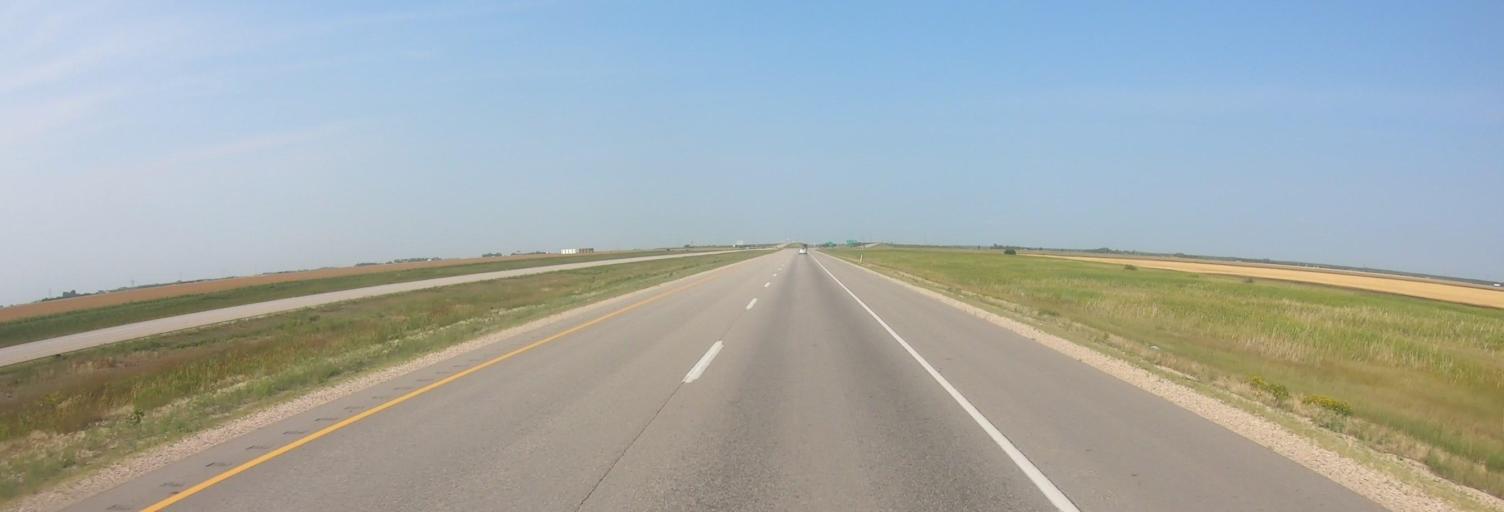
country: CA
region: Manitoba
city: Steinbach
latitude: 49.6890
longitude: -96.6548
